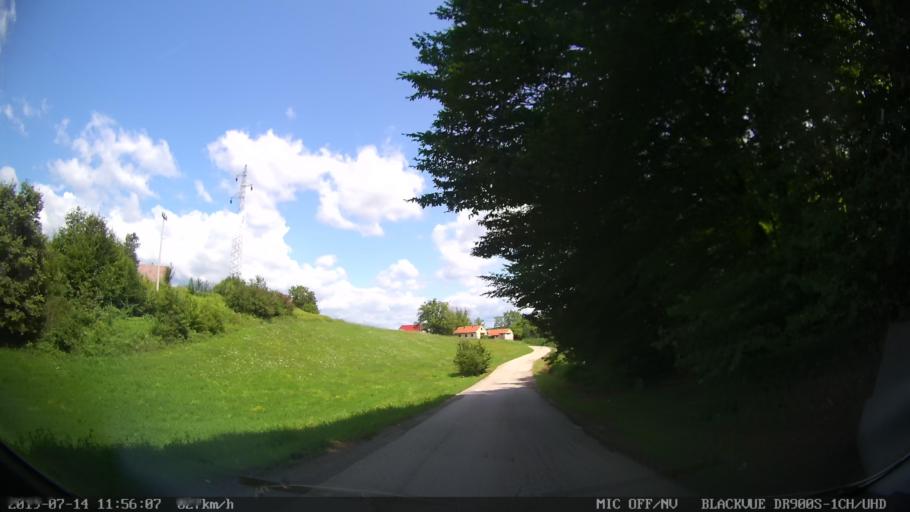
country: HR
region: Karlovacka
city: Vojnic
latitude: 45.3855
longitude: 15.6073
